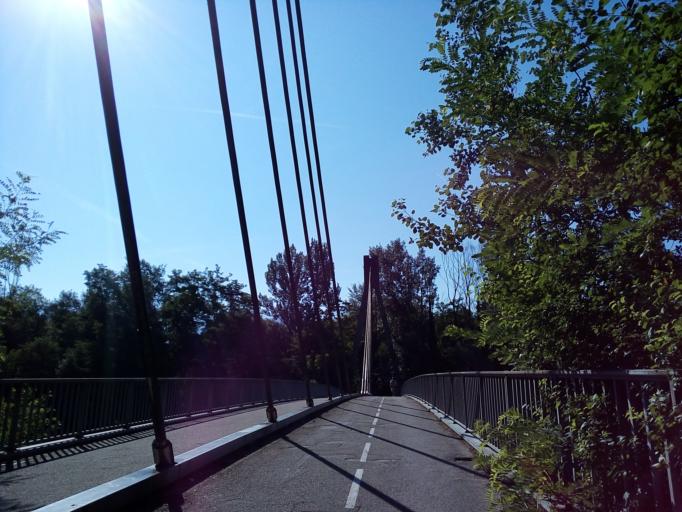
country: FR
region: Rhone-Alpes
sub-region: Departement de l'Isere
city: Corenc
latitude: 45.1988
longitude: 5.7695
